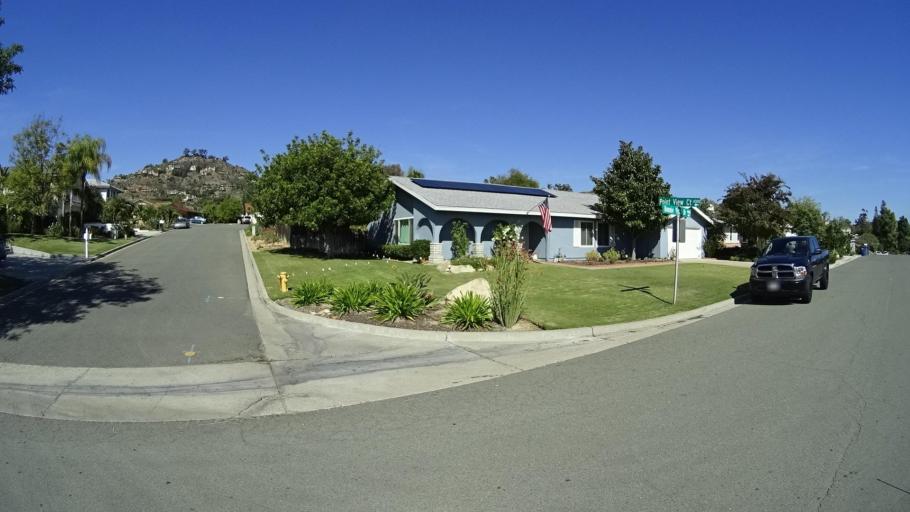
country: US
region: California
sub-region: San Diego County
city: Casa de Oro-Mount Helix
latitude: 32.7575
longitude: -116.9822
